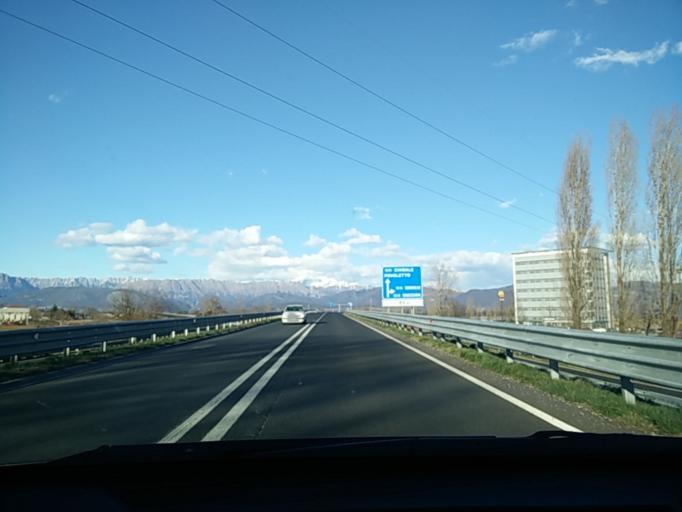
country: IT
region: Friuli Venezia Giulia
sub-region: Provincia di Udine
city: Tavagnacco
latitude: 46.1206
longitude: 13.2235
